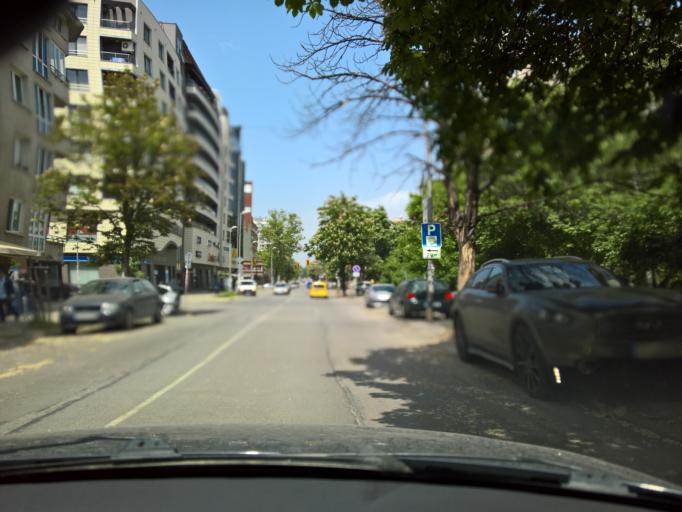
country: BG
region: Sofia-Capital
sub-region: Stolichna Obshtina
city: Sofia
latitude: 42.6787
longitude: 23.3607
